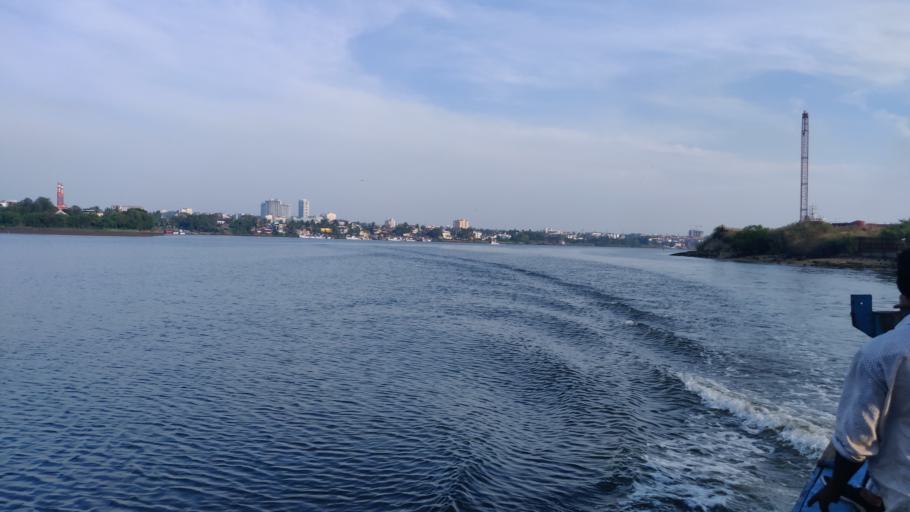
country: IN
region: Karnataka
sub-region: Dakshina Kannada
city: Mangalore
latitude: 12.8777
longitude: 74.8216
